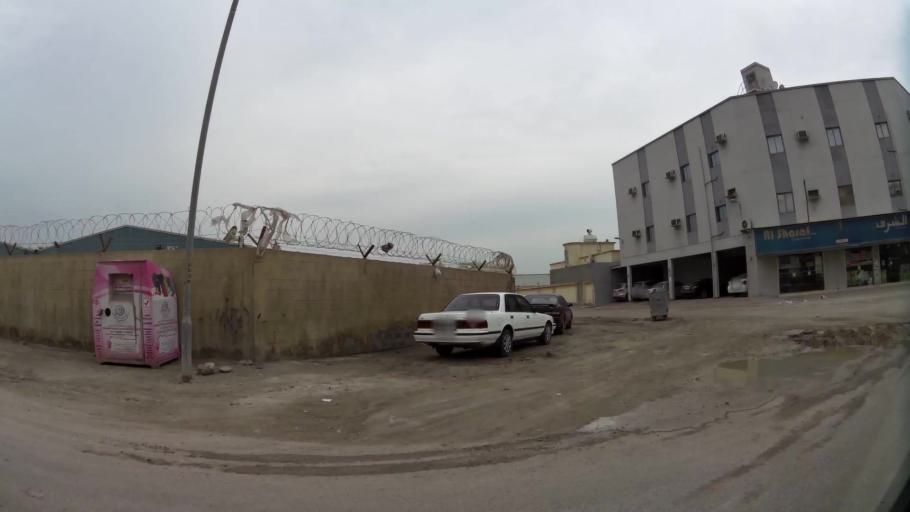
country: BH
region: Northern
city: Sitrah
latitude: 26.1432
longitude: 50.6010
